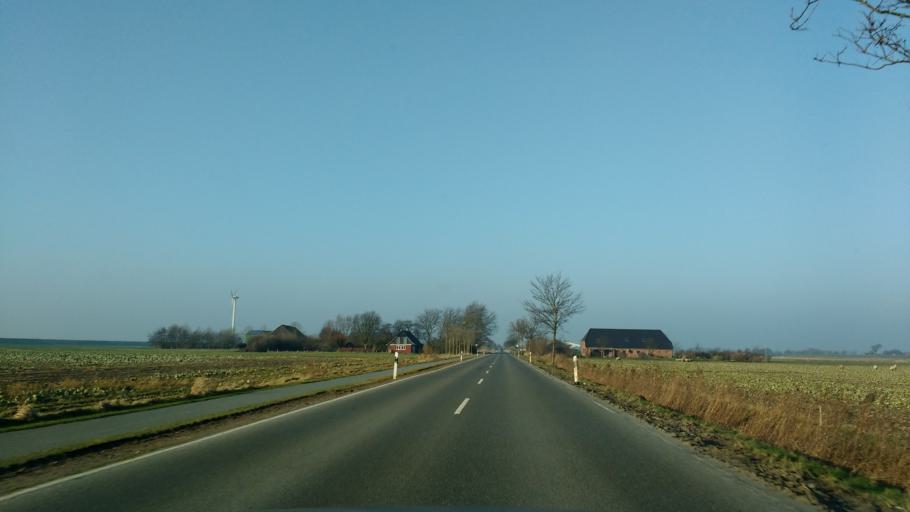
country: DE
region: Schleswig-Holstein
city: Friedrichskoog
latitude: 53.9920
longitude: 8.9019
